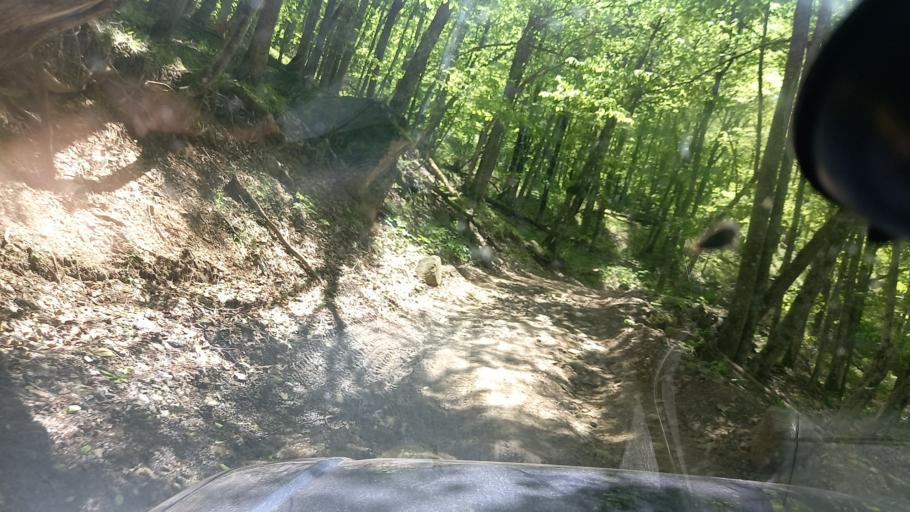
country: RU
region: Krasnodarskiy
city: Tuapse
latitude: 44.2512
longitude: 39.2825
